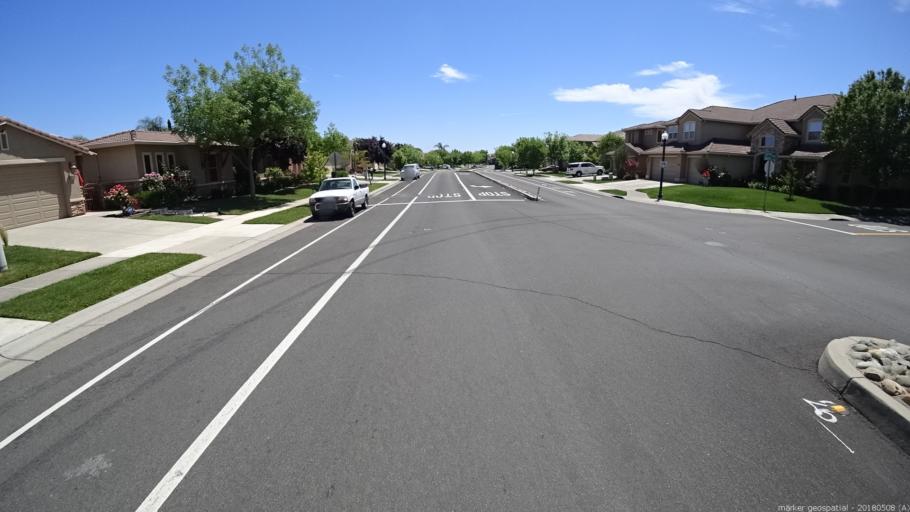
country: US
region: California
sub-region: Sacramento County
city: Elverta
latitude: 38.6790
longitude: -121.5218
